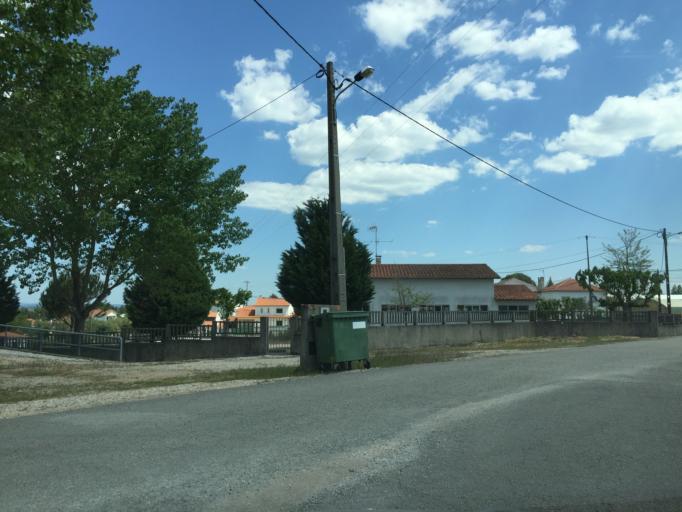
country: PT
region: Santarem
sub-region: Ourem
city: Ourem
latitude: 39.6788
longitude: -8.5661
